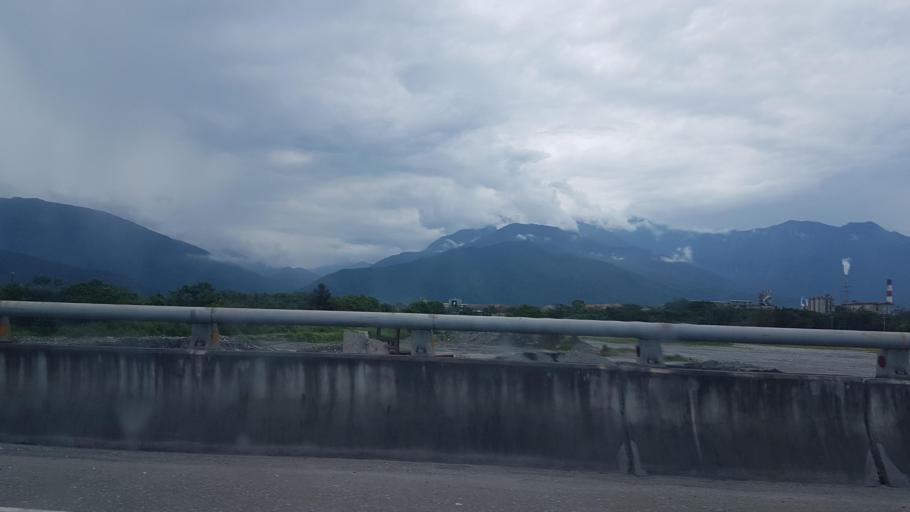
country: TW
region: Taiwan
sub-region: Hualien
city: Hualian
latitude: 23.9215
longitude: 121.5866
